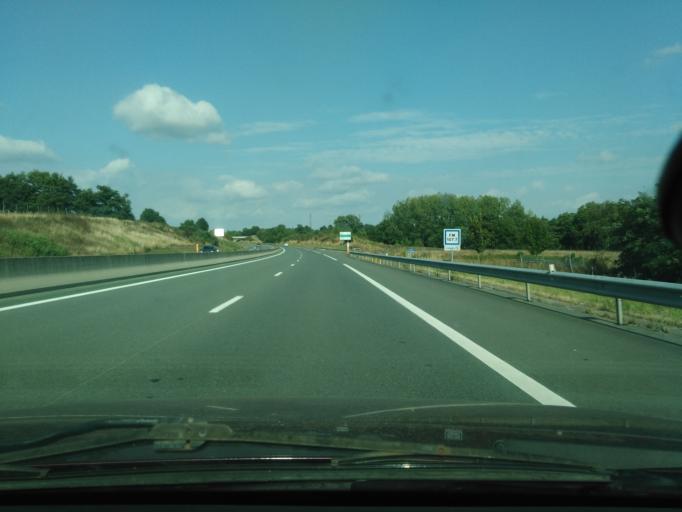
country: FR
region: Pays de la Loire
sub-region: Departement de la Vendee
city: Nesmy
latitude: 46.6283
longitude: -1.4138
